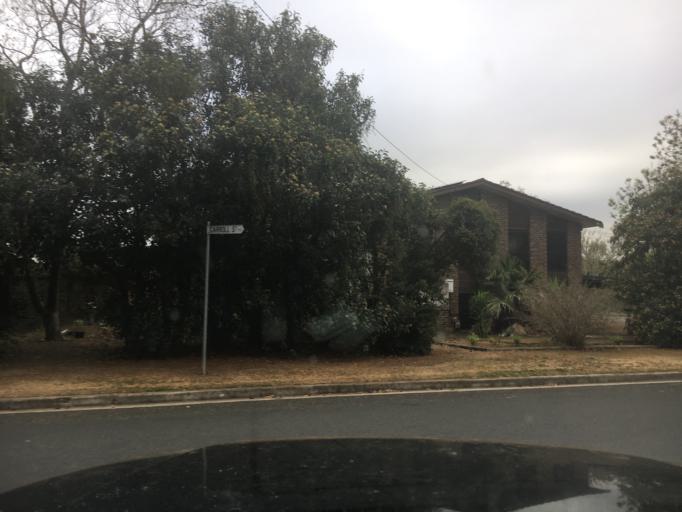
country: AU
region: New South Wales
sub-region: Singleton
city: Singleton
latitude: -32.5665
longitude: 151.1874
